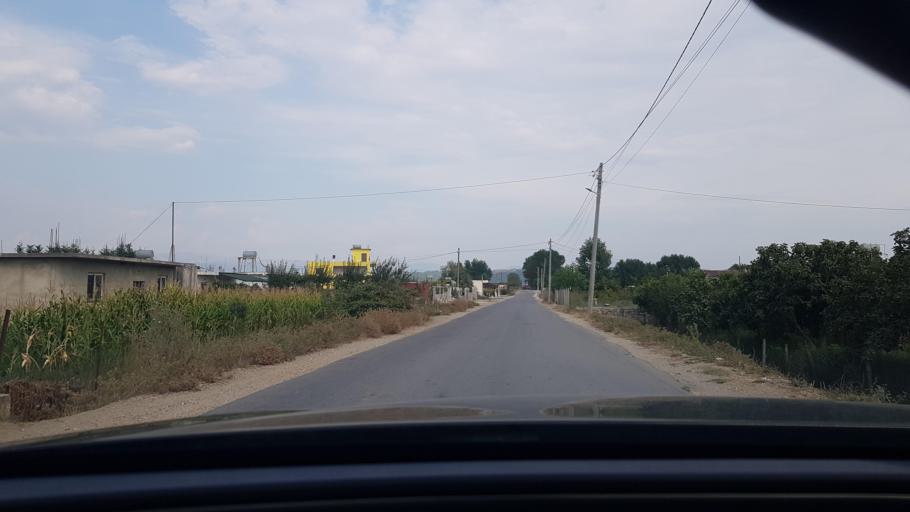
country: AL
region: Durres
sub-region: Rrethi i Durresit
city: Katundi i Ri
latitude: 41.4856
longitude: 19.5232
